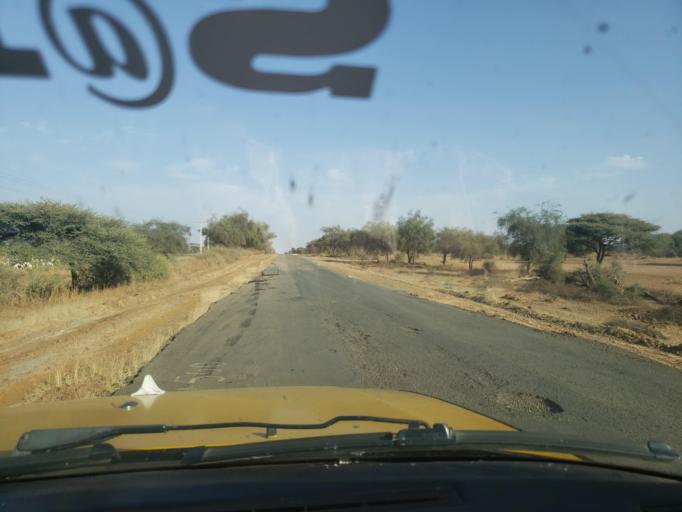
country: SN
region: Louga
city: Louga
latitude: 15.5039
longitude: -15.9522
